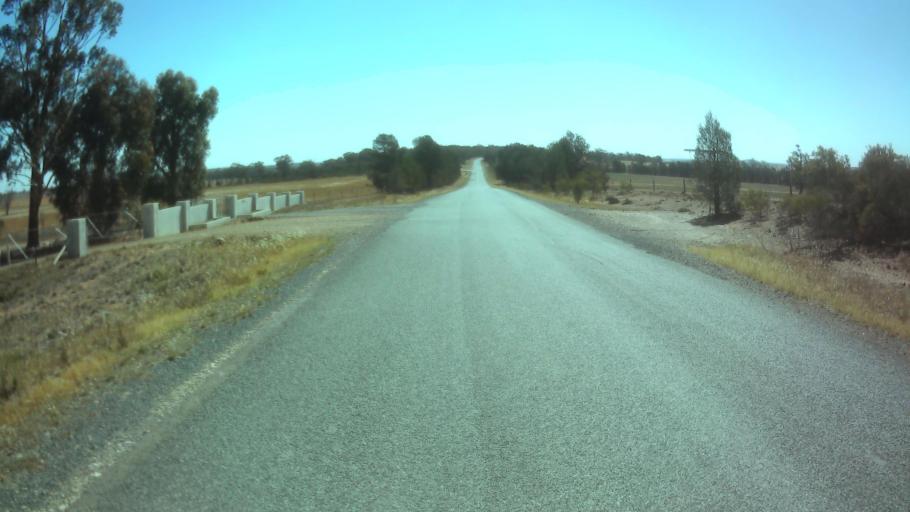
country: AU
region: New South Wales
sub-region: Weddin
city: Grenfell
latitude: -33.7545
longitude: 147.8355
